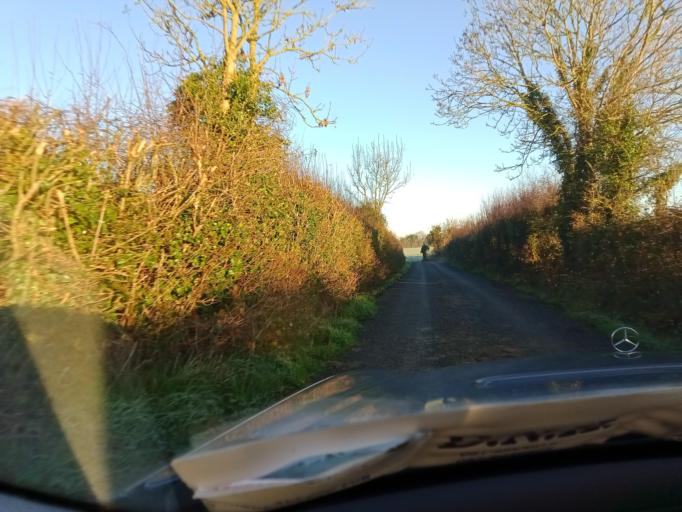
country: IE
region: Leinster
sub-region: Kilkenny
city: Callan
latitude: 52.5140
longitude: -7.4458
